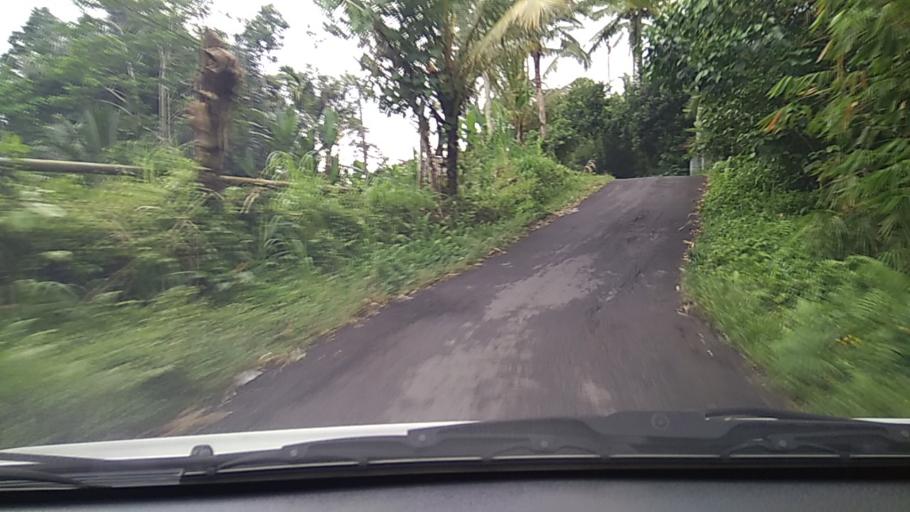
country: ID
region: Bali
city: Banjar Dujung Kaja
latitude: -8.4124
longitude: 115.2859
